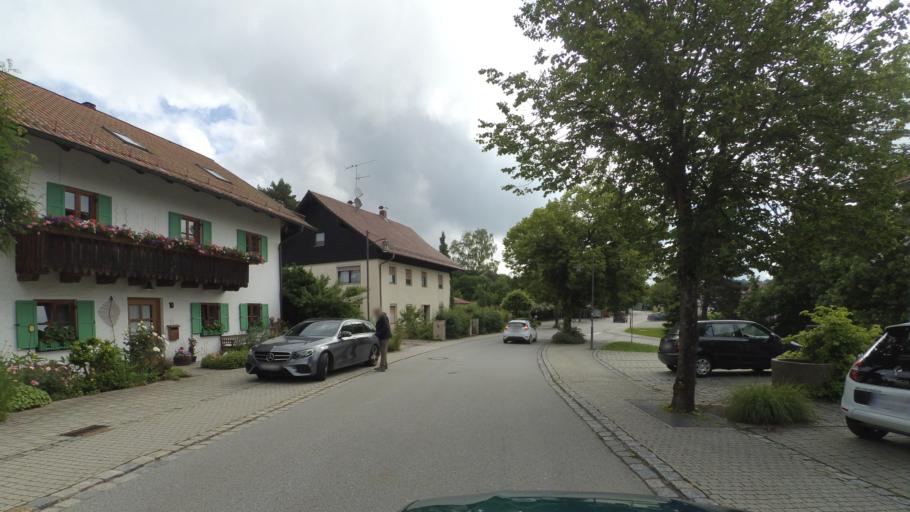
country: DE
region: Bavaria
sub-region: Lower Bavaria
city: Mitterfels
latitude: 48.9731
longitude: 12.6775
